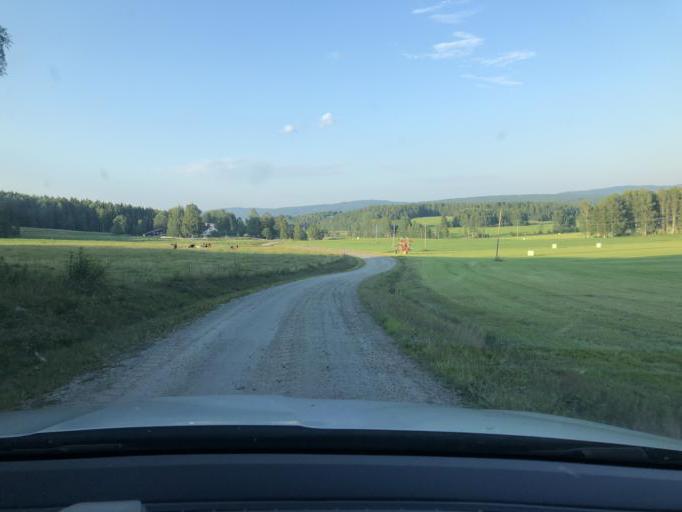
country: SE
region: Vaesternorrland
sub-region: Kramfors Kommun
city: Bollstabruk
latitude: 63.0534
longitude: 17.7258
